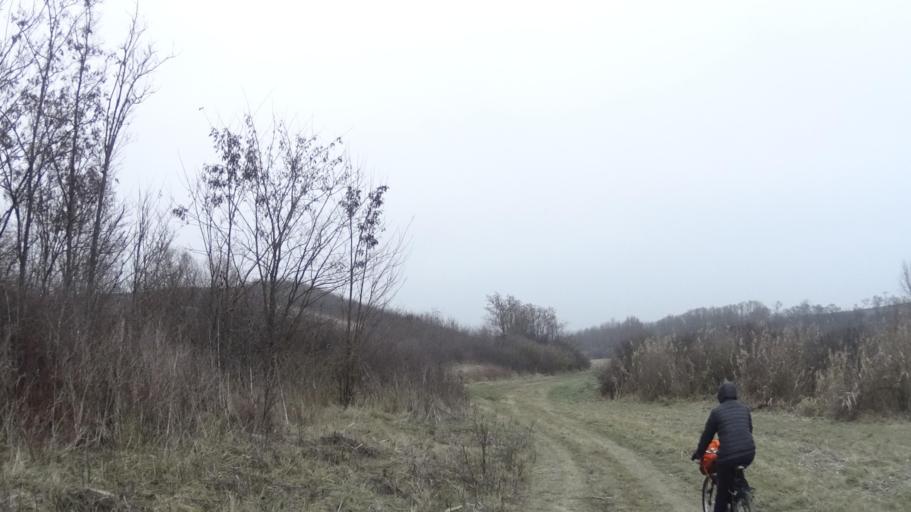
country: HU
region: Pest
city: Kosd
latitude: 47.7798
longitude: 19.2198
